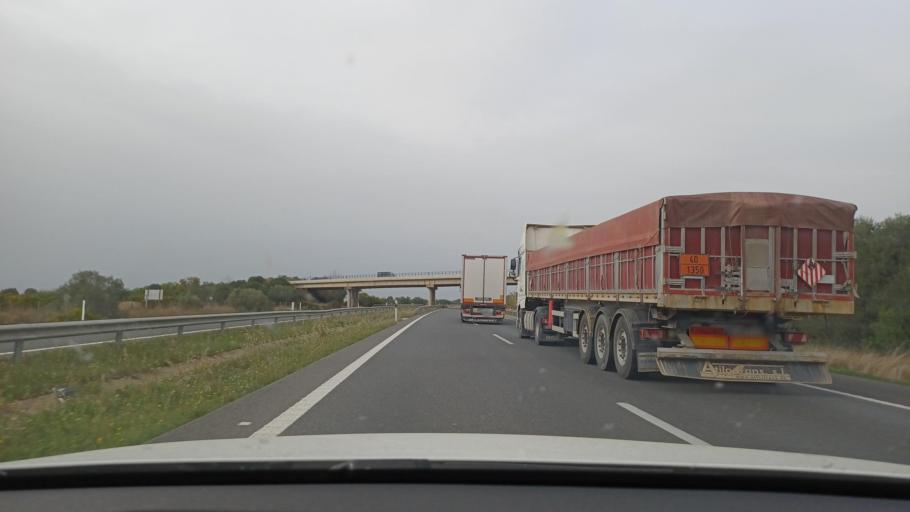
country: ES
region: Valencia
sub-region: Provincia de Castello
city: Vinaros
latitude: 40.4894
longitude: 0.4152
